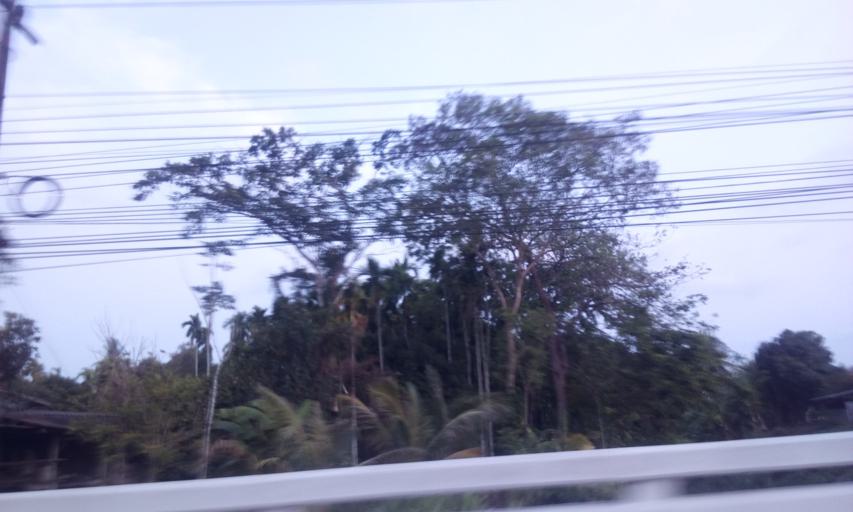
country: TH
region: Trat
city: Khao Saming
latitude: 12.3067
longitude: 102.3480
